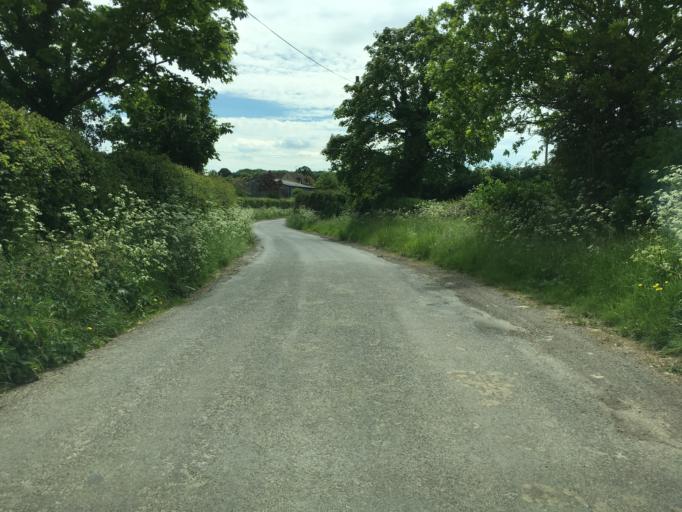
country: GB
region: England
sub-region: South Gloucestershire
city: Charfield
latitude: 51.6656
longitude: -2.4101
